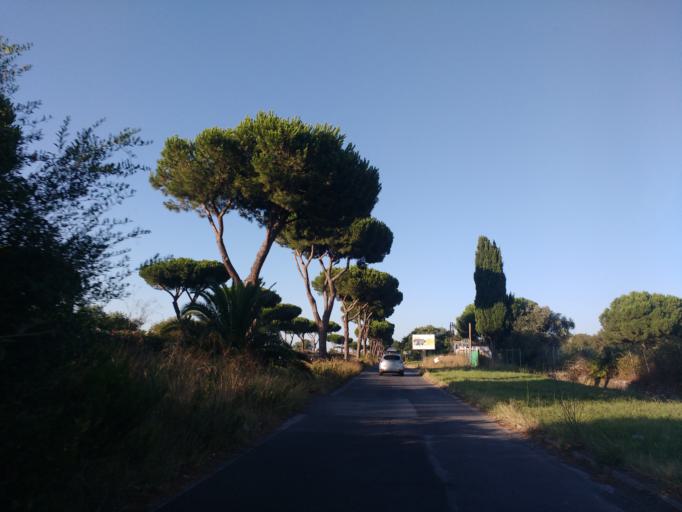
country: IT
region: Latium
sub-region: Citta metropolitana di Roma Capitale
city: Acilia-Castel Fusano-Ostia Antica
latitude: 41.7565
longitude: 12.3722
